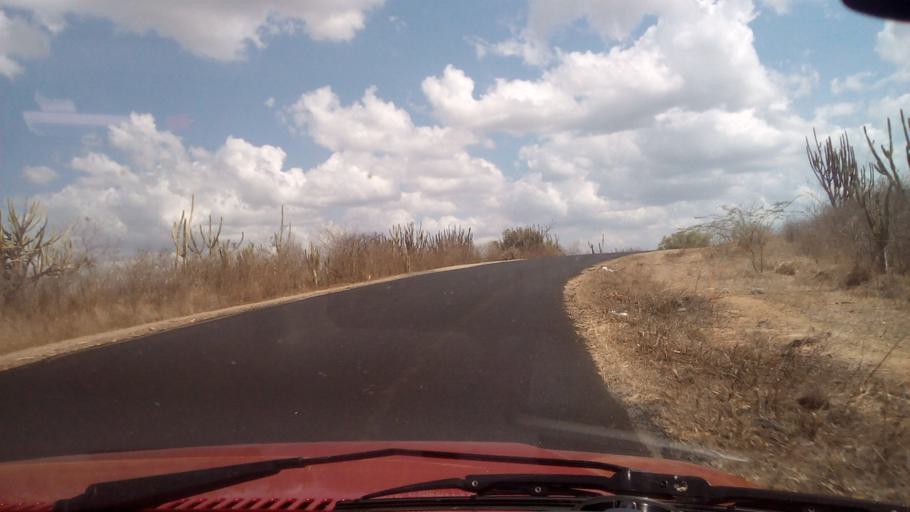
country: BR
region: Paraiba
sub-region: Bananeiras
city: Bananeiras
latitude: -6.7208
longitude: -35.7133
